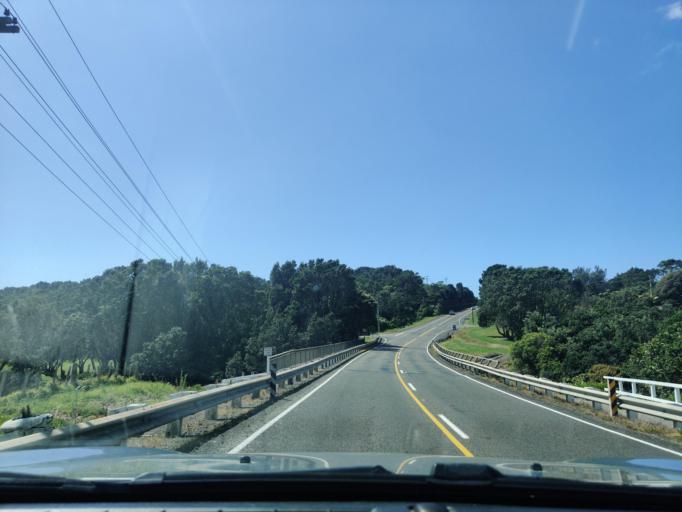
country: NZ
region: Taranaki
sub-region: New Plymouth District
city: New Plymouth
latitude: -39.1124
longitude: 173.9587
